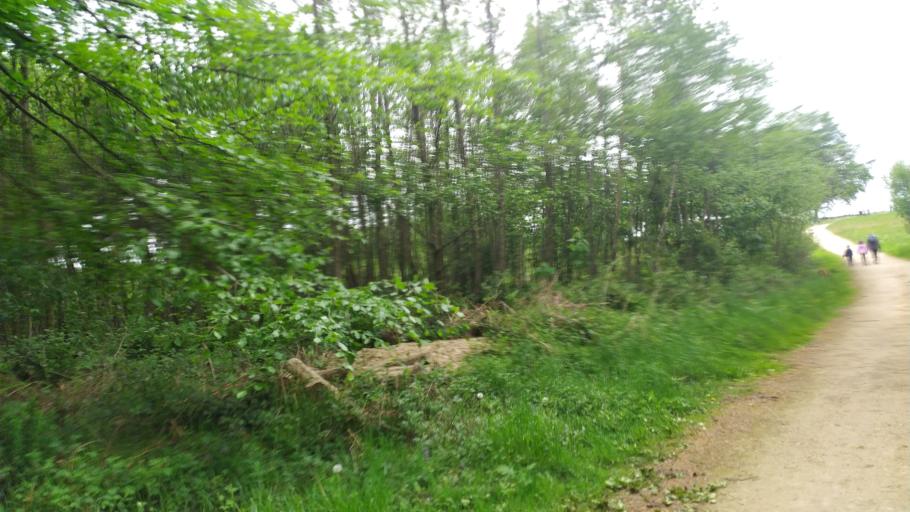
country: GB
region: England
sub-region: City and Borough of Leeds
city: Bramham
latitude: 53.8589
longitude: -1.3842
